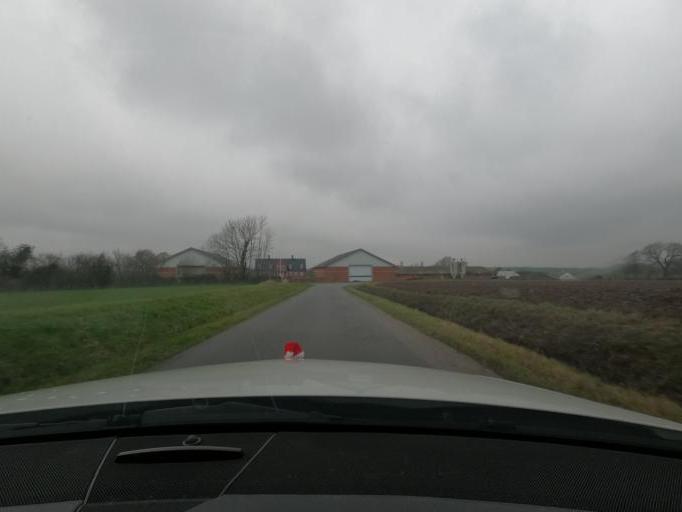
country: DK
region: South Denmark
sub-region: Haderslev Kommune
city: Starup
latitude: 55.1988
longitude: 9.6405
